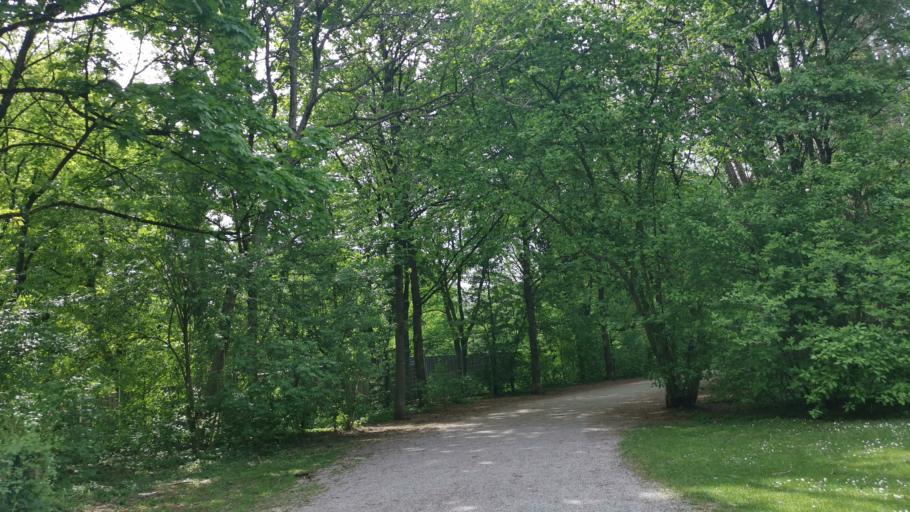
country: DE
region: Bavaria
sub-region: Upper Bavaria
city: Bogenhausen
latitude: 48.1718
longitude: 11.5916
